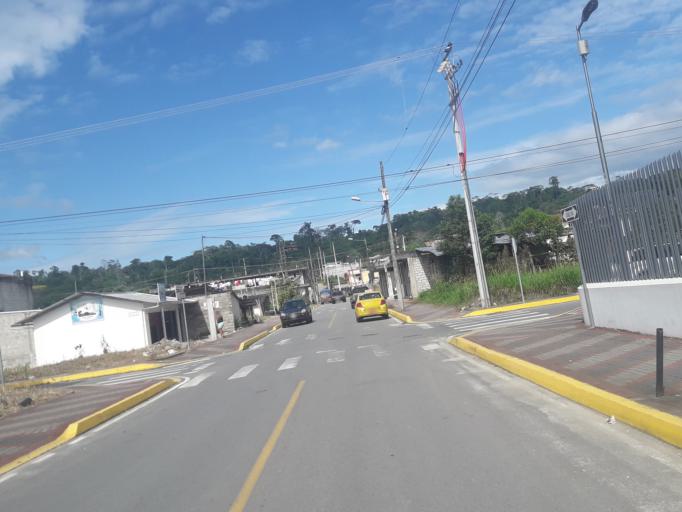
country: EC
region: Napo
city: Tena
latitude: -1.0080
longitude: -77.8141
